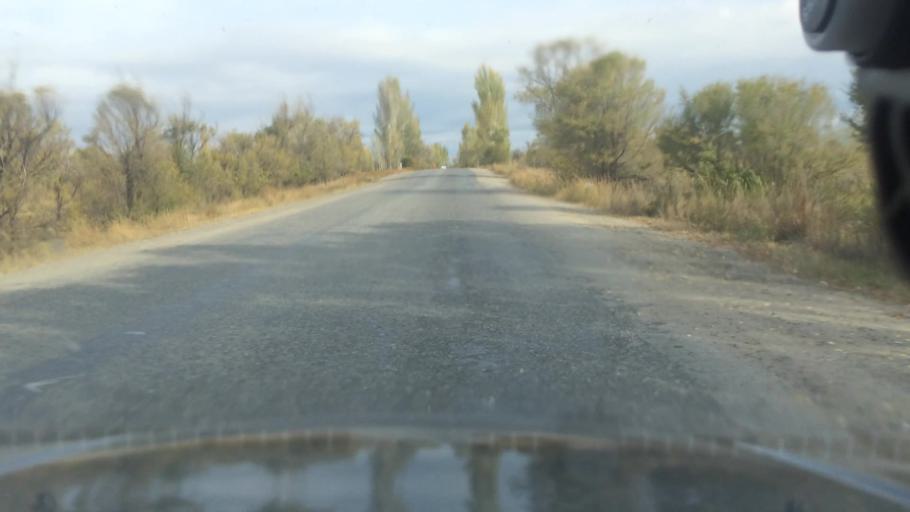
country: KG
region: Ysyk-Koel
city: Karakol
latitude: 42.5682
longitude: 78.3911
